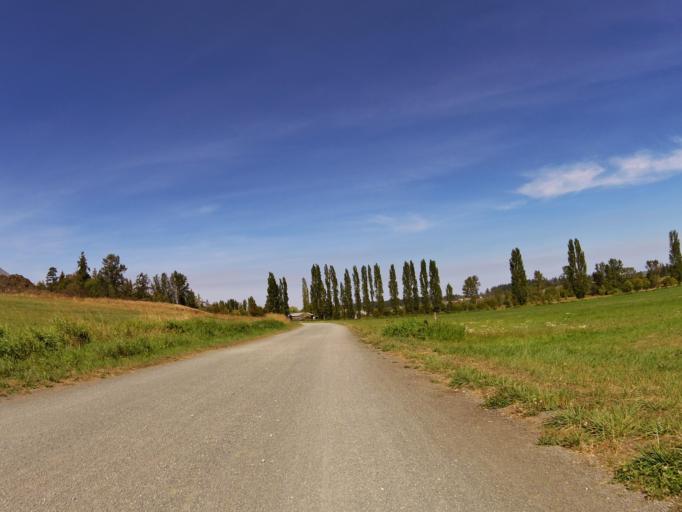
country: CA
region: British Columbia
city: North Saanich
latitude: 48.5560
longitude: -123.3864
